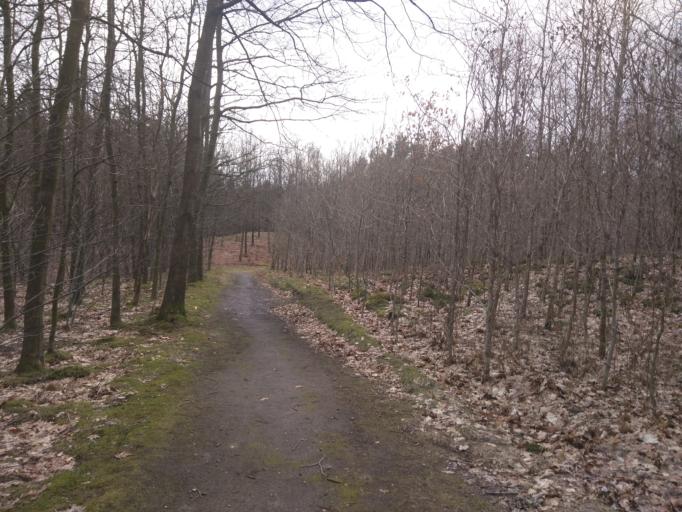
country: DK
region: Central Jutland
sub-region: Silkeborg Kommune
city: Silkeborg
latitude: 56.1815
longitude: 9.5268
